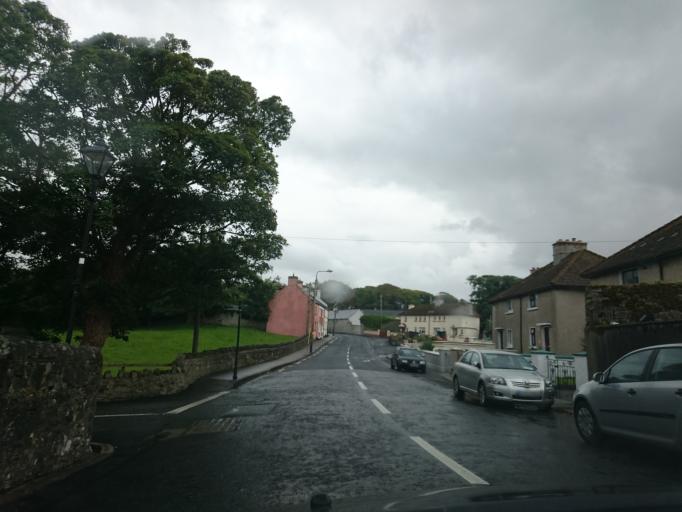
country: IE
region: Connaught
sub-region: Maigh Eo
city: Ballina
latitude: 54.2122
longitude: -9.2197
